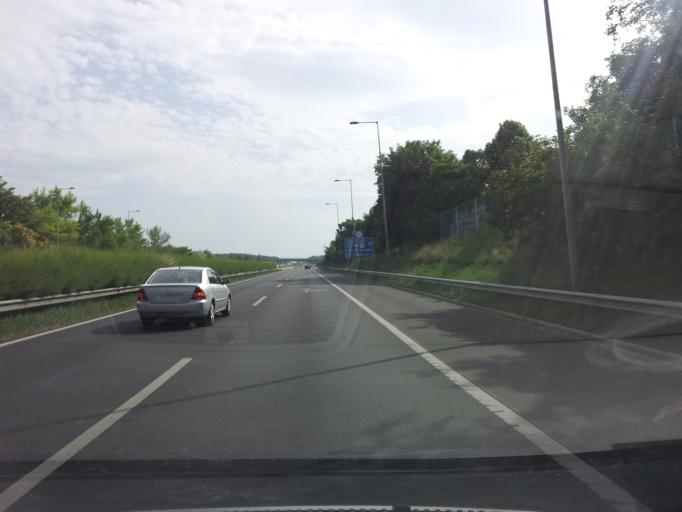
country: HU
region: Pest
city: Toeroekbalint
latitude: 47.4391
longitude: 18.9022
